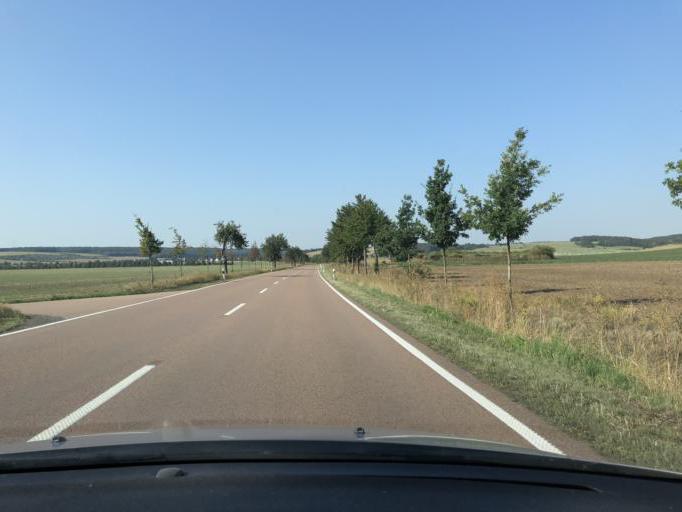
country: DE
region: Saxony-Anhalt
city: Krumpa
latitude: 51.2521
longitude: 11.8461
